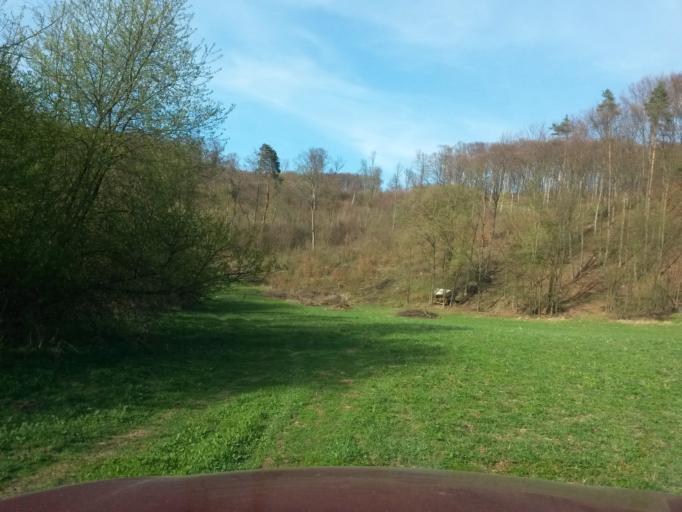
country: SK
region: Presovsky
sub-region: Okres Presov
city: Presov
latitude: 48.9025
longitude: 21.2099
